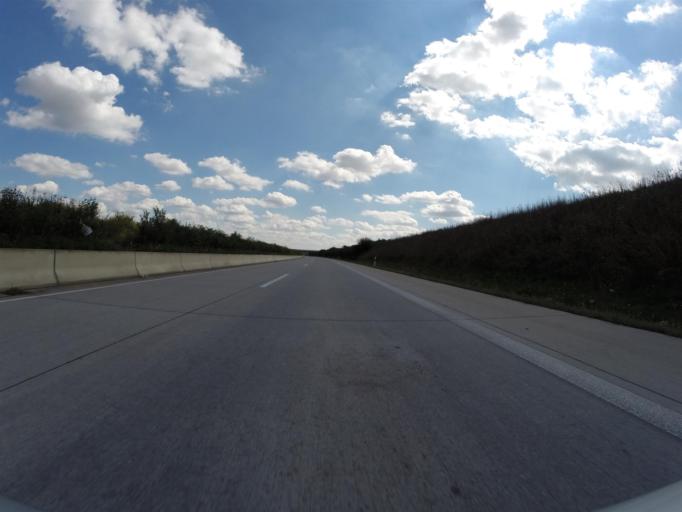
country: DE
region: Thuringia
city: Zimmernsupra
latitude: 50.9744
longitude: 10.9160
